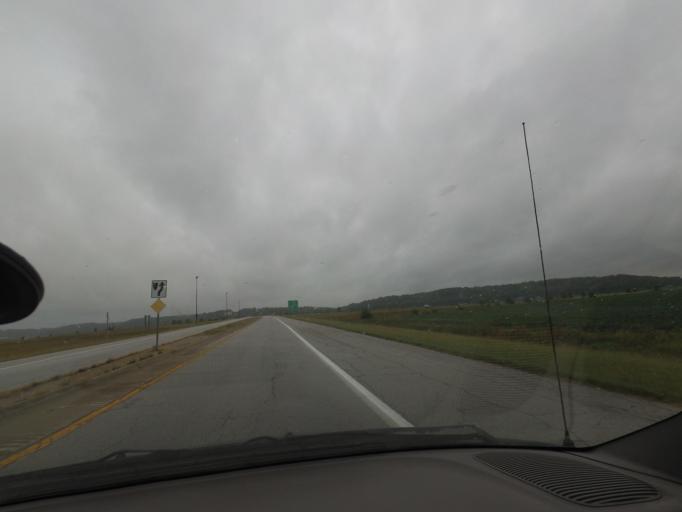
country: US
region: Illinois
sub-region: Adams County
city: Payson
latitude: 39.7158
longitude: -91.1949
